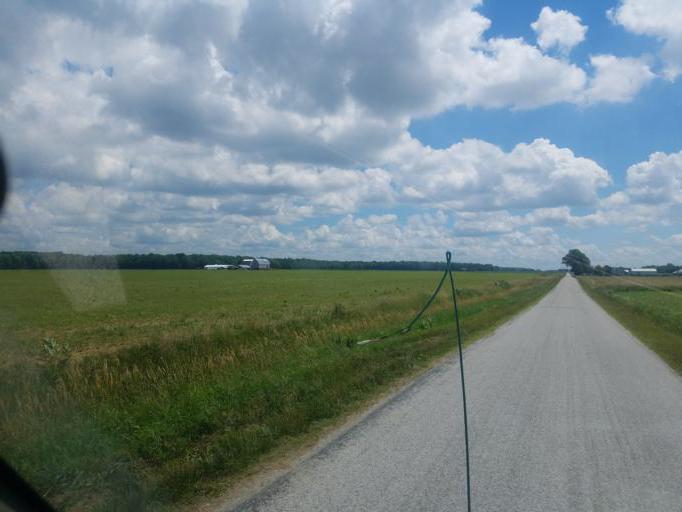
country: US
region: Ohio
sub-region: Huron County
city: Willard
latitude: 40.9958
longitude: -82.8349
